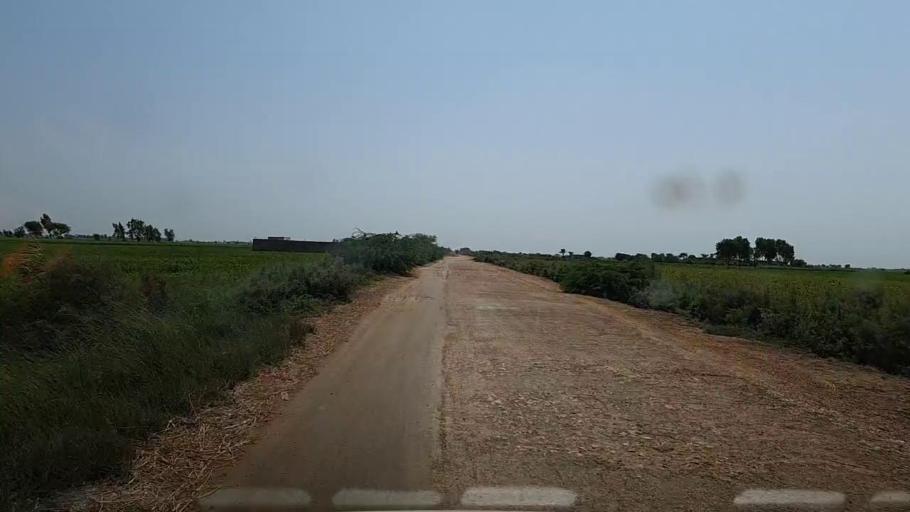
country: PK
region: Sindh
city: Mirpur Batoro
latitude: 24.6269
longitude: 68.4522
